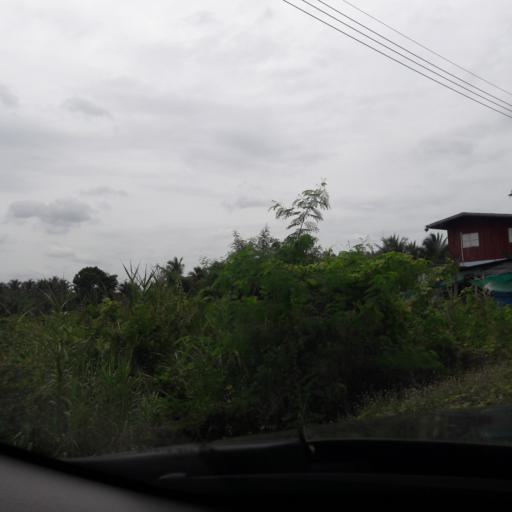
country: TH
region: Ratchaburi
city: Damnoen Saduak
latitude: 13.5768
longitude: 99.9366
